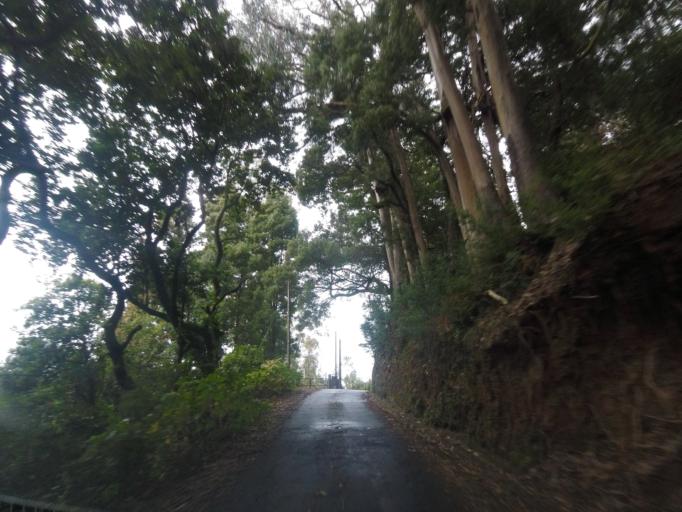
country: PT
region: Madeira
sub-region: Santana
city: Santana
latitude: 32.7855
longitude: -16.8983
